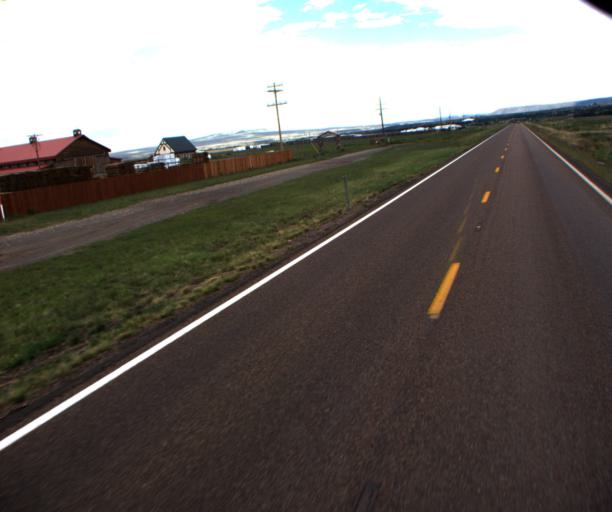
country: US
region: Arizona
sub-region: Apache County
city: Eagar
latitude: 34.1084
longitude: -109.3339
